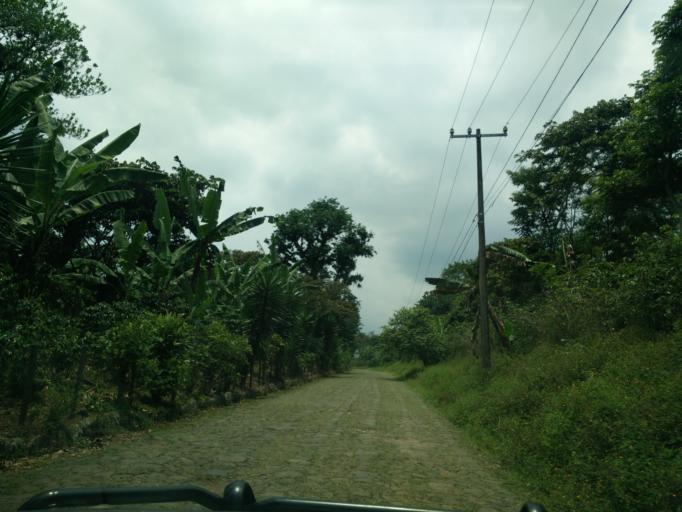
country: MX
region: Veracruz
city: Xico
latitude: 19.4092
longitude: -96.9902
